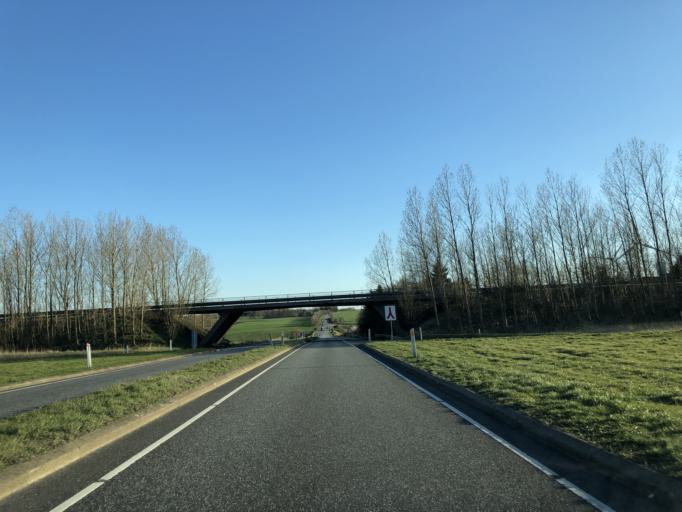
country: DK
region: North Denmark
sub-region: Vesthimmerland Kommune
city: Alestrup
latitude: 56.6955
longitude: 9.5348
